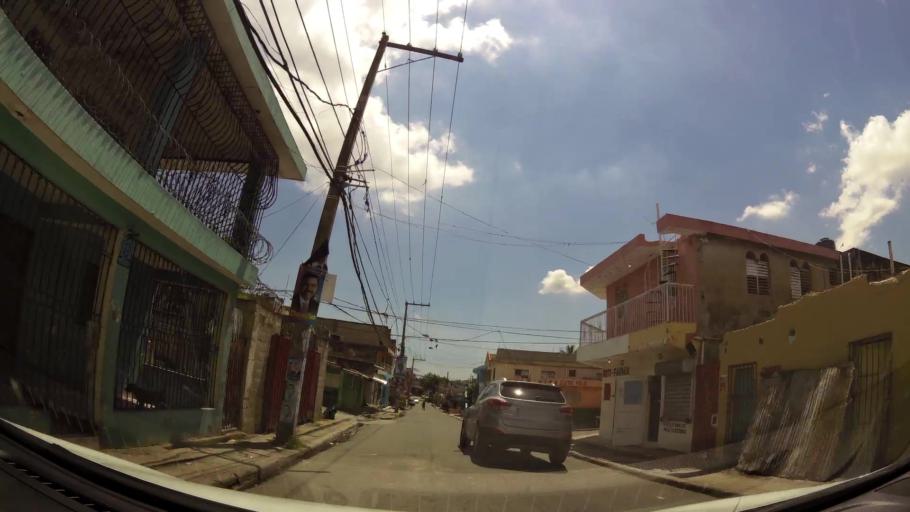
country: DO
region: Santo Domingo
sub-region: Santo Domingo
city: Santo Domingo Este
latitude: 18.5397
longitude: -69.8631
